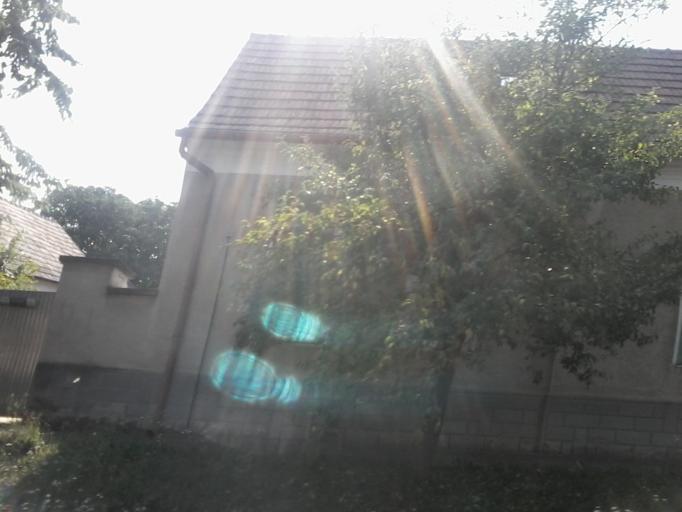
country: HU
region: Vas
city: Celldomolk
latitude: 47.2099
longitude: 17.1044
